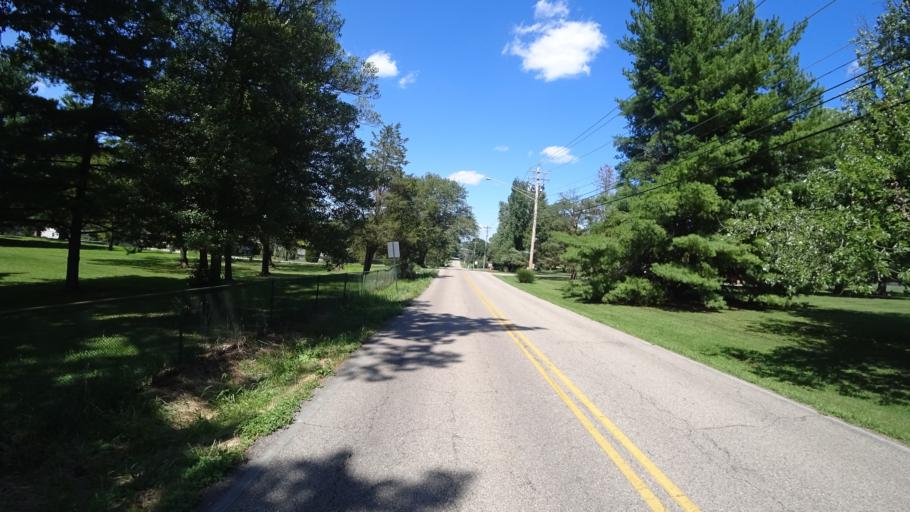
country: US
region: Ohio
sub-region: Butler County
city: New Miami
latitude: 39.4081
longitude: -84.5266
